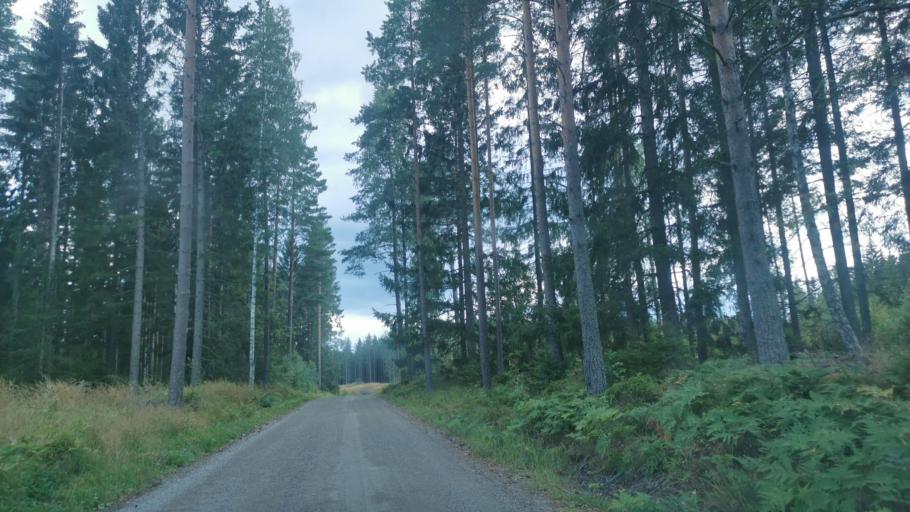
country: SE
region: OEstergoetland
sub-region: Finspangs Kommun
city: Finspang
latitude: 58.7985
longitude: 15.7746
